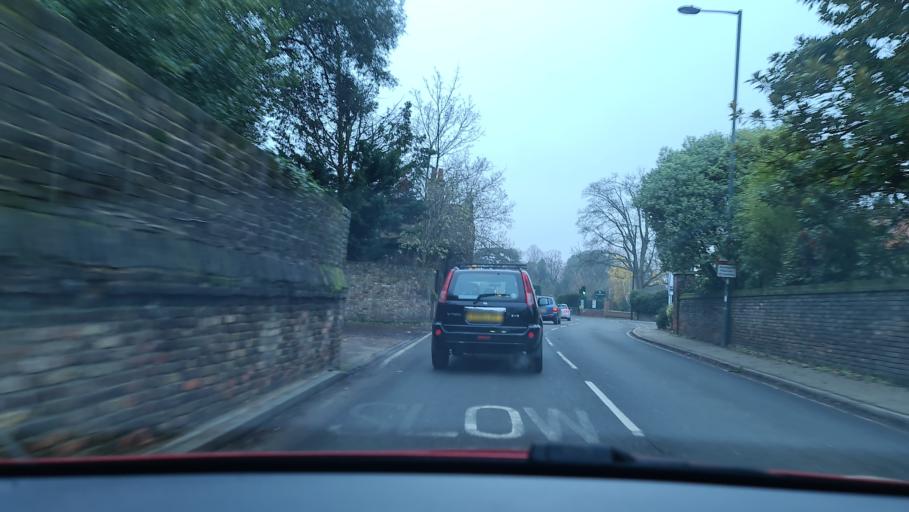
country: GB
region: England
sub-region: Greater London
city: Richmond
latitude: 51.4457
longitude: -0.3031
